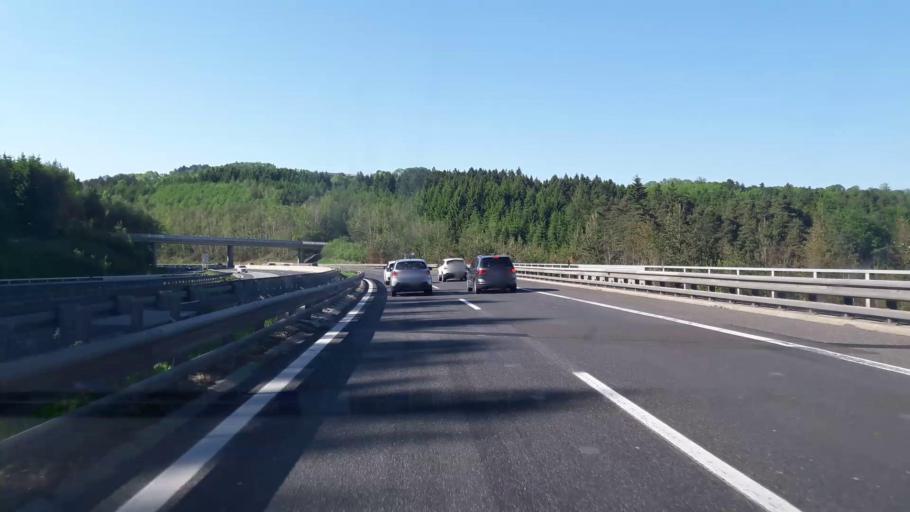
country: AT
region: Lower Austria
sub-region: Politischer Bezirk Neunkirchen
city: Thomasberg
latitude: 47.5533
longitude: 16.1301
